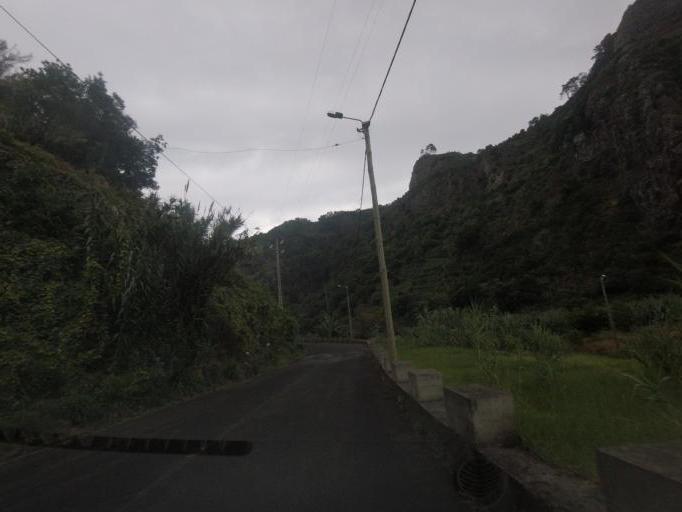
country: PT
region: Madeira
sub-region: Santana
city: Santana
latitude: 32.8228
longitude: -16.8982
